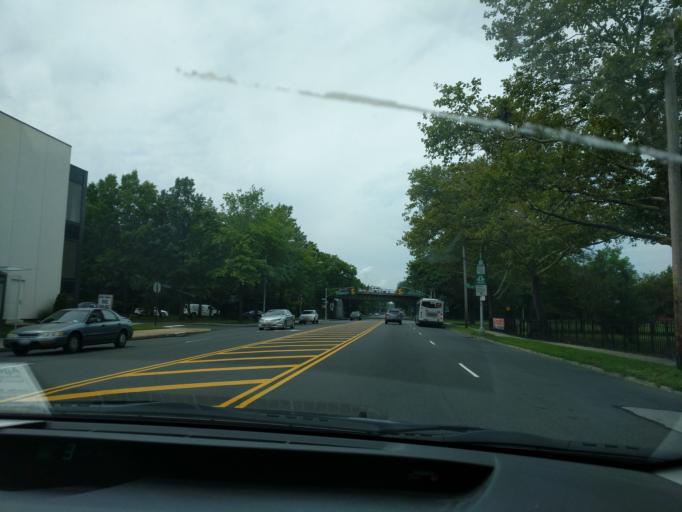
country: US
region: New York
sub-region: Richmond County
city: Bloomfield
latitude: 40.6098
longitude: -74.1484
